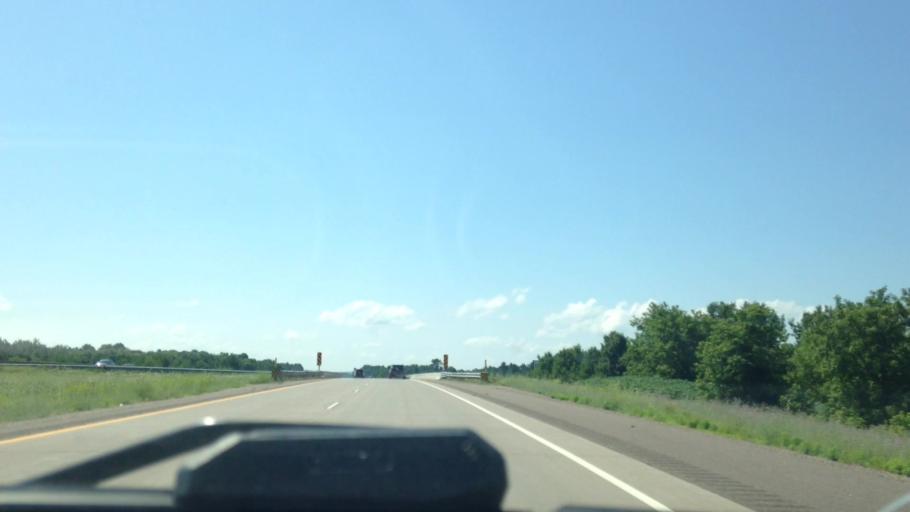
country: US
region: Wisconsin
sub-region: Barron County
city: Cameron
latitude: 45.4093
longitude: -91.7633
